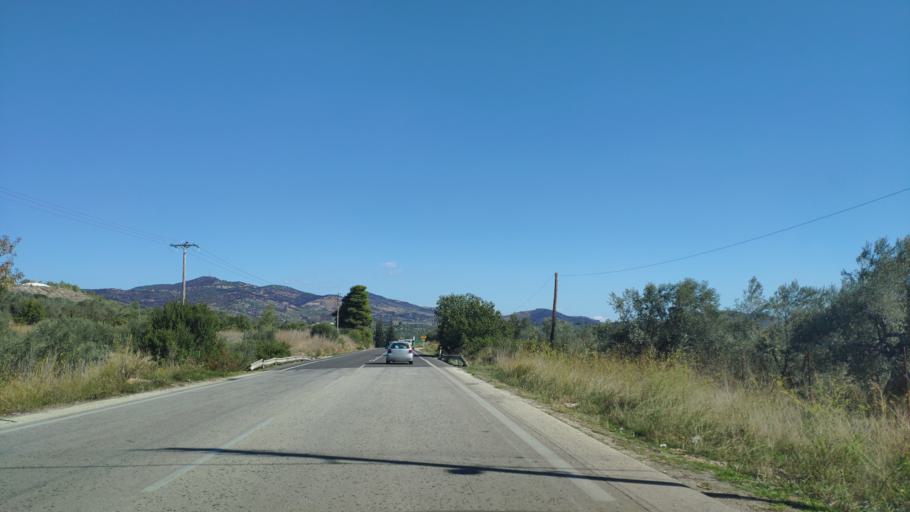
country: GR
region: Peloponnese
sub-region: Nomos Korinthias
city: Khiliomodhi
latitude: 37.8331
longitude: 22.8929
